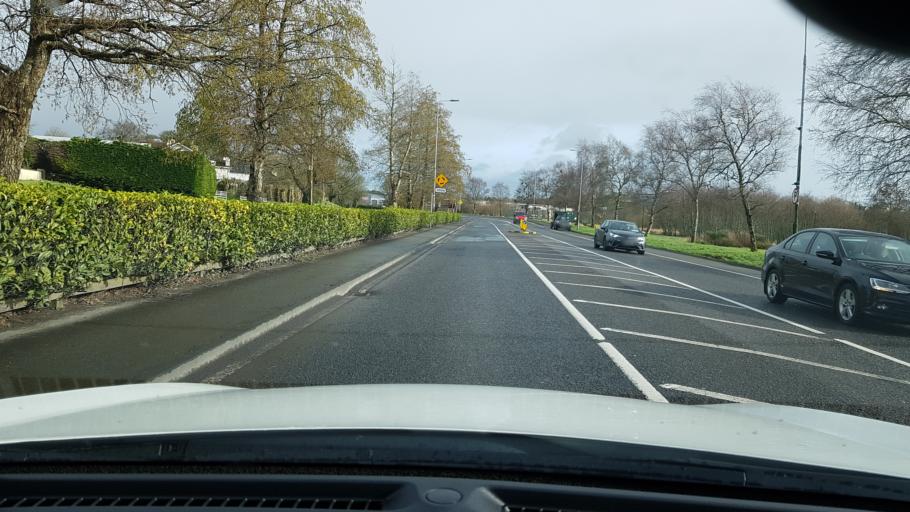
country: IE
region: Connaught
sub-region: County Leitrim
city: Carrick-on-Shannon
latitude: 53.9436
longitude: -8.0891
